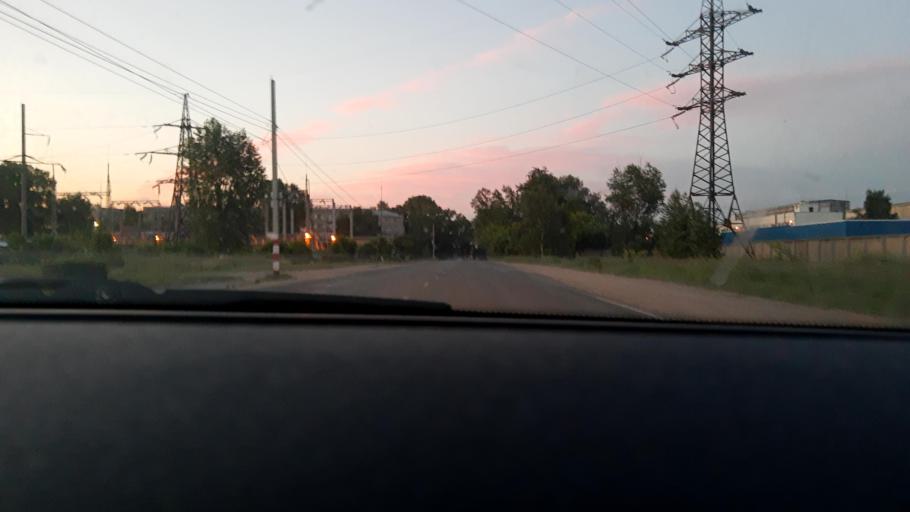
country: RU
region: Nizjnij Novgorod
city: Bor
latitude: 56.3400
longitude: 44.0956
